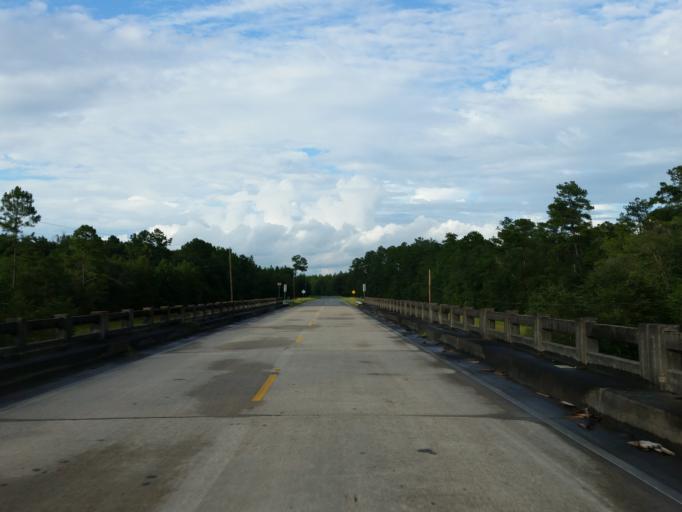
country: US
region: Florida
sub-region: Hamilton County
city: Jasper
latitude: 30.6556
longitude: -82.5637
